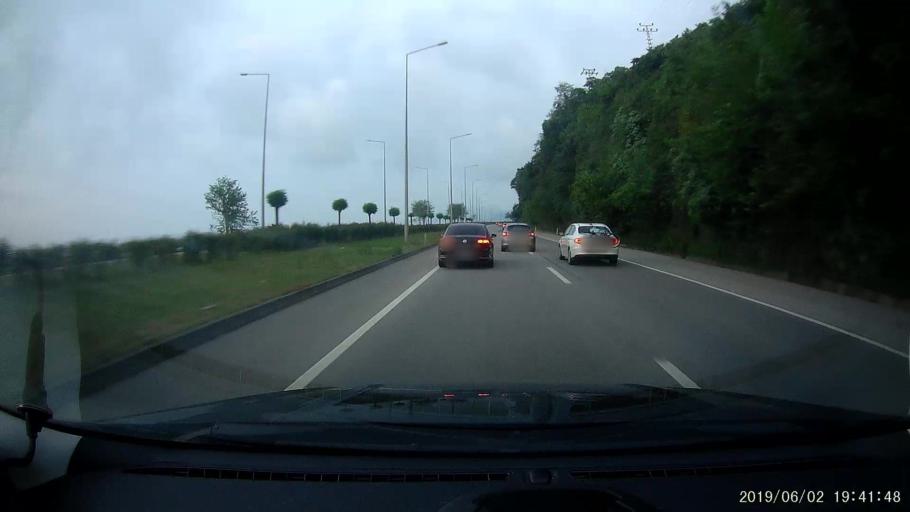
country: TR
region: Giresun
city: Kesap
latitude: 40.9145
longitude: 38.4882
